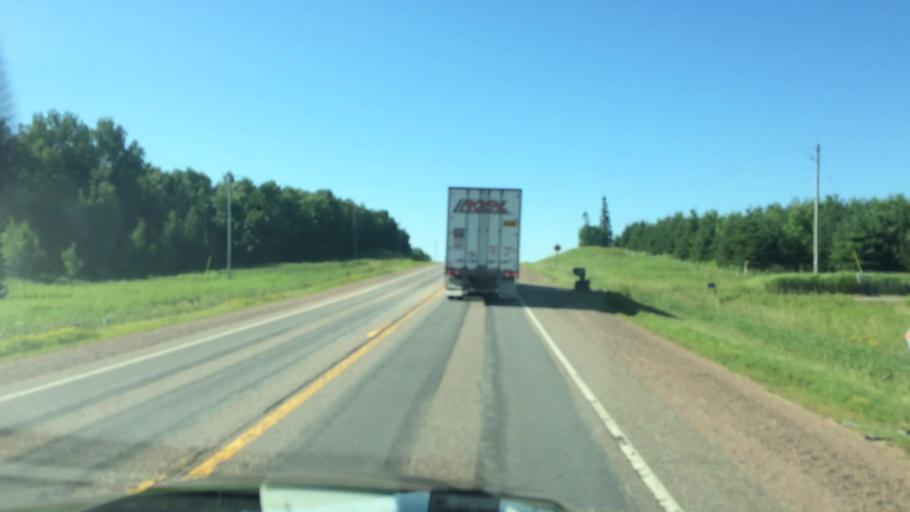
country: US
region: Wisconsin
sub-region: Marathon County
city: Athens
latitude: 44.9272
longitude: -90.0788
